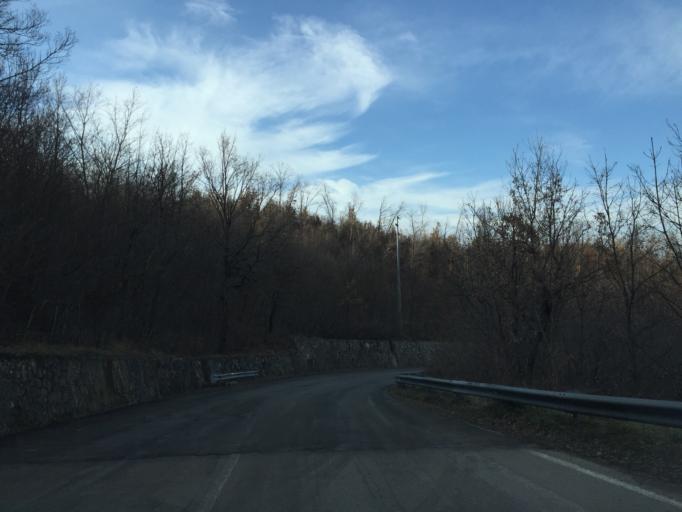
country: IT
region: Molise
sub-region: Provincia di Campobasso
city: San Massimo
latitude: 41.4830
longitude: 14.4094
